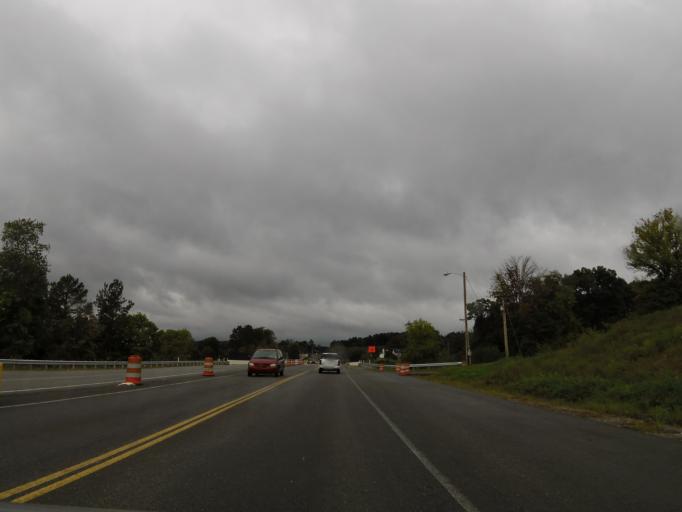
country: US
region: Tennessee
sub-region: Loudon County
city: Lenoir City
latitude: 35.7939
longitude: -84.2535
